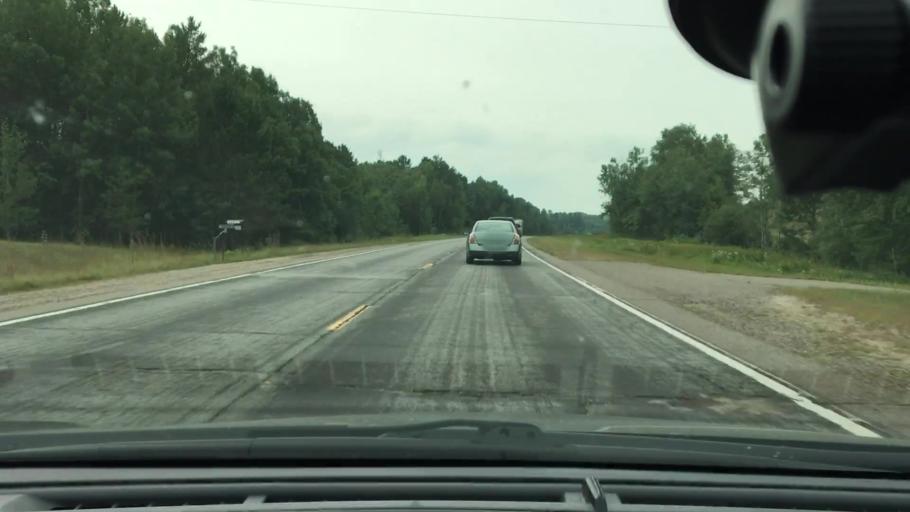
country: US
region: Minnesota
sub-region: Crow Wing County
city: Cross Lake
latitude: 46.6700
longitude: -93.9517
